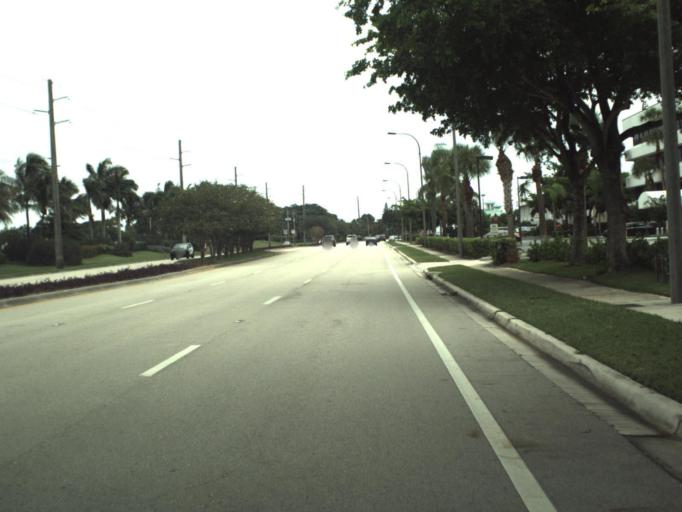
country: US
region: Florida
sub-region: Palm Beach County
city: North Palm Beach
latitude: 26.8227
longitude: -80.0597
